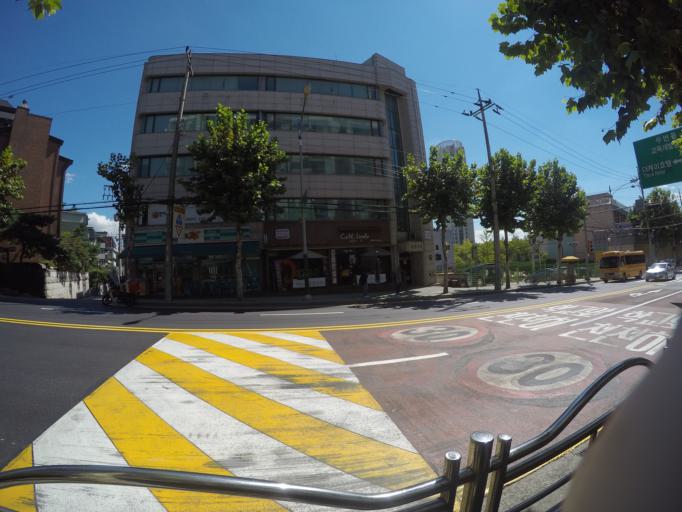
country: KR
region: Seoul
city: Seoul
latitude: 37.4749
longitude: 127.0327
